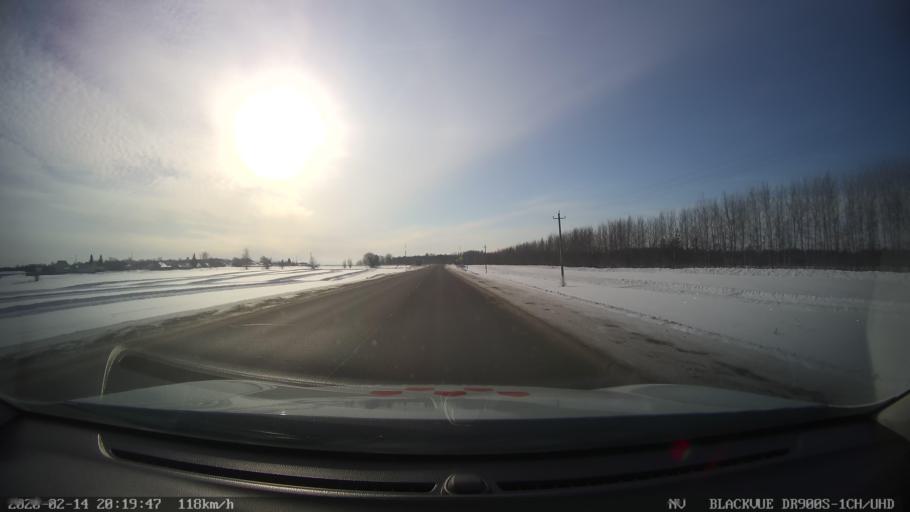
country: RU
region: Tatarstan
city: Verkhniy Uslon
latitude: 55.5655
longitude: 48.9014
